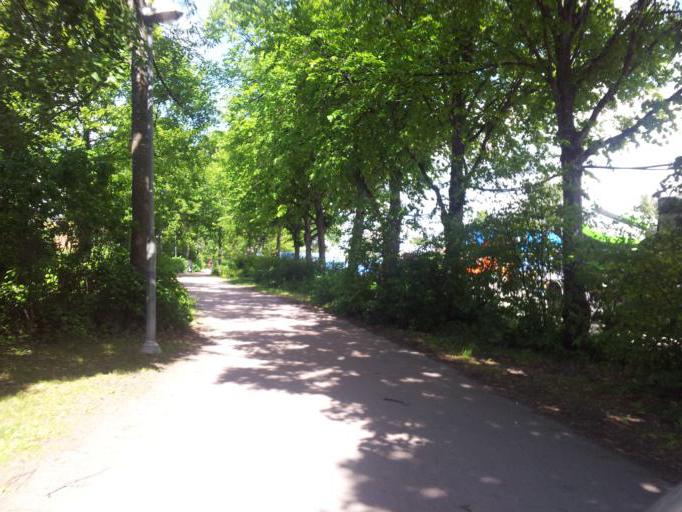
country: SE
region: Uppsala
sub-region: Uppsala Kommun
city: Uppsala
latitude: 59.8670
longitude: 17.6480
